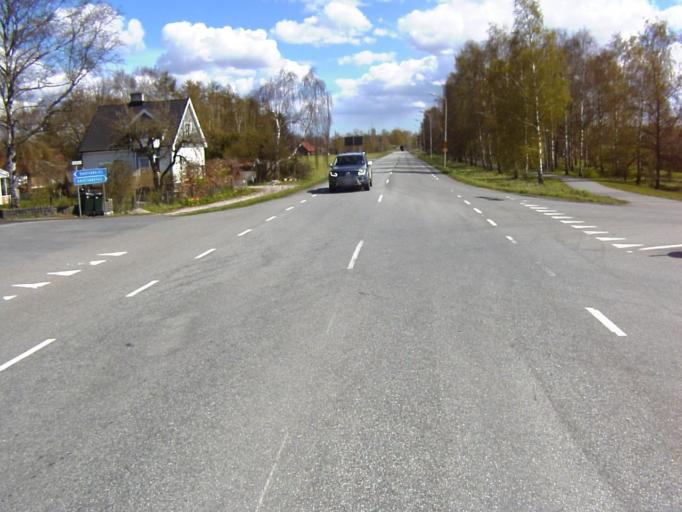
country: SE
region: Skane
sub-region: Kristianstads Kommun
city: Kristianstad
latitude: 56.0165
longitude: 14.1063
